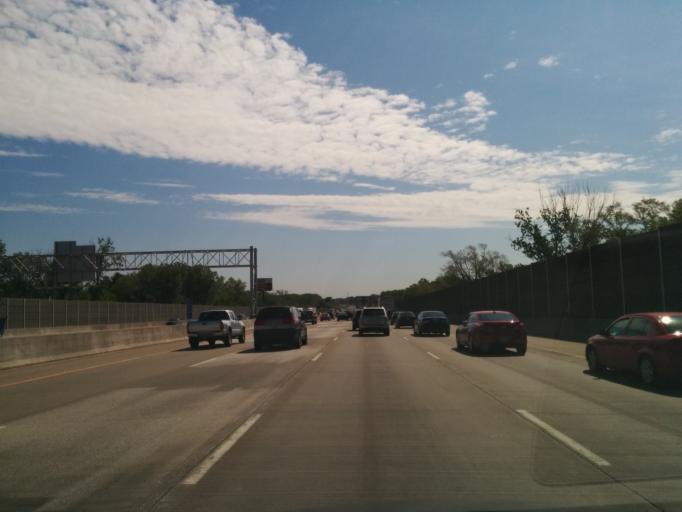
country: US
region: Indiana
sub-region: Lake County
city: New Chicago
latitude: 41.5728
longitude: -87.2803
